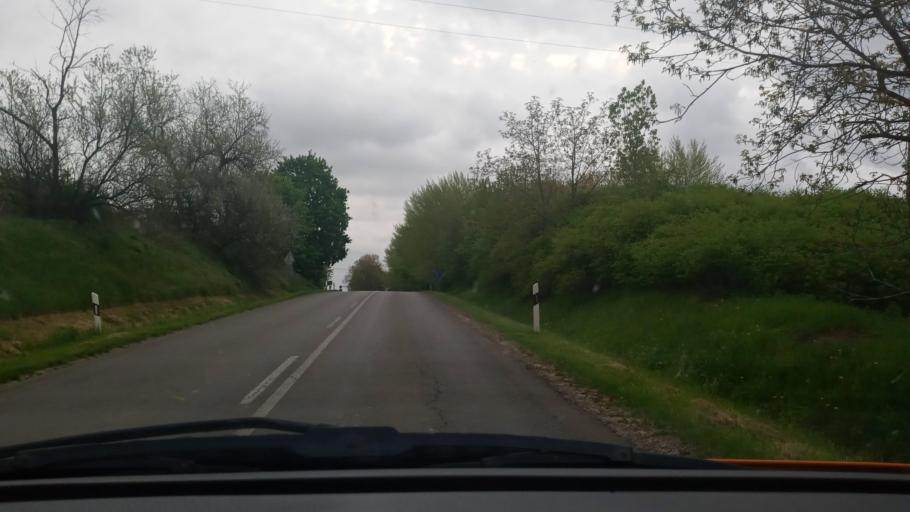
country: HU
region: Baranya
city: Boly
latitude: 45.9880
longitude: 18.5148
